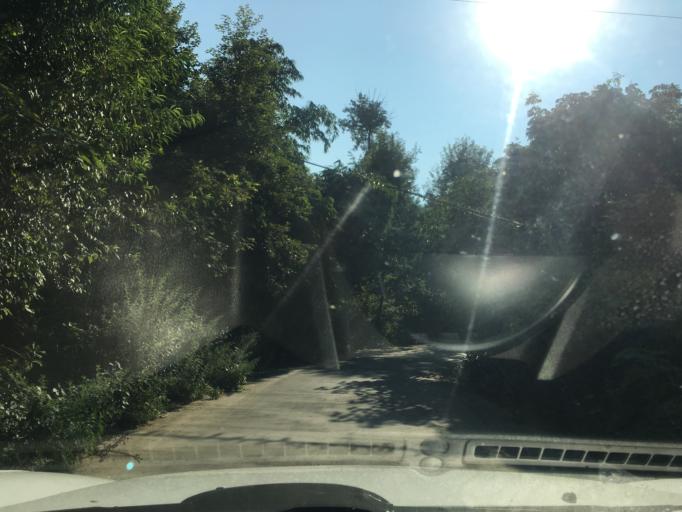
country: CN
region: Guangxi Zhuangzu Zizhiqu
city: Xinzhou
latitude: 25.4397
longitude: 105.7495
